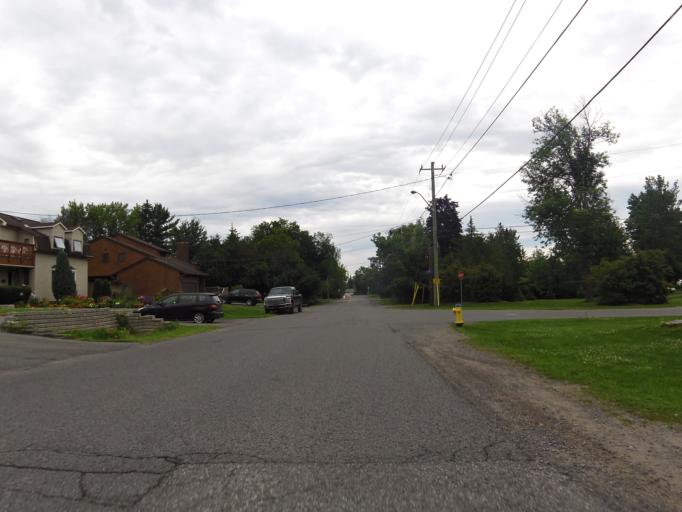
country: CA
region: Ontario
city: Bells Corners
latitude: 45.3561
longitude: -75.8496
